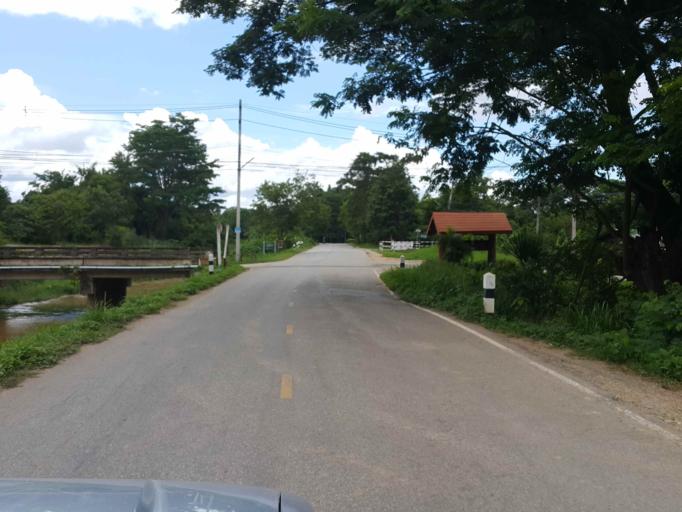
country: TH
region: Chiang Mai
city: San Sai
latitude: 18.9062
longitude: 98.9395
